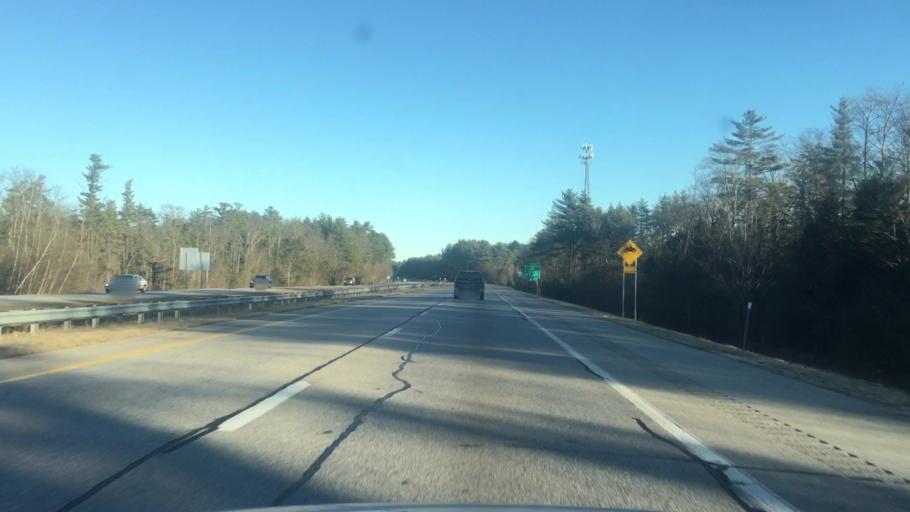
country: US
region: New Hampshire
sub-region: Rockingham County
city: Epping
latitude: 43.0254
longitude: -71.1025
